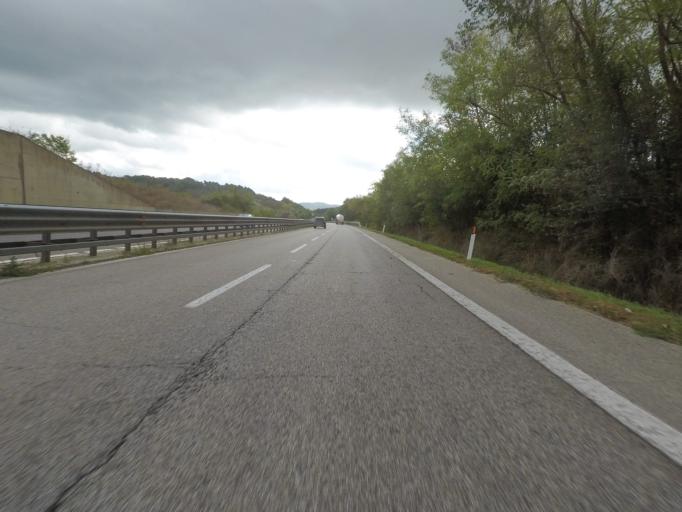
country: IT
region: Tuscany
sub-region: Provincia di Siena
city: Rapolano Terme
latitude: 43.3165
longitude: 11.5742
